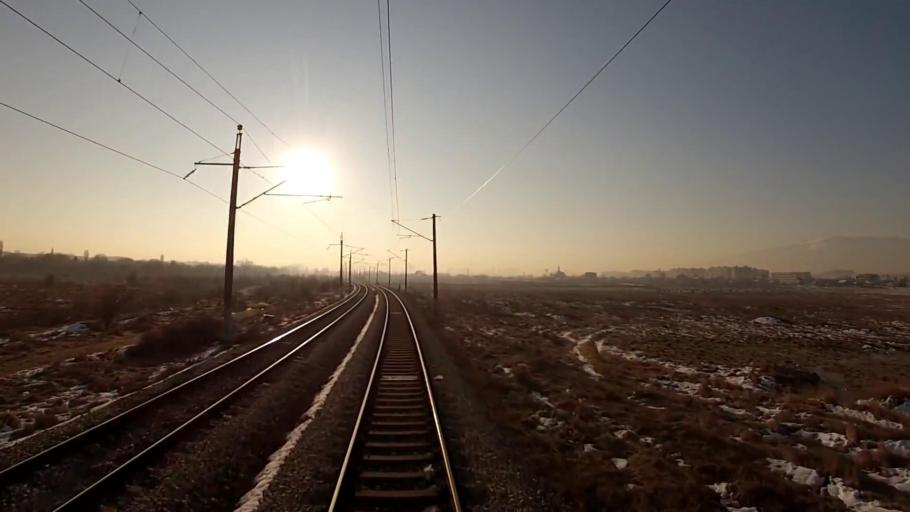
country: BG
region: Sofiya
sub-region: Obshtina Bozhurishte
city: Bozhurishte
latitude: 42.7427
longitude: 23.2591
